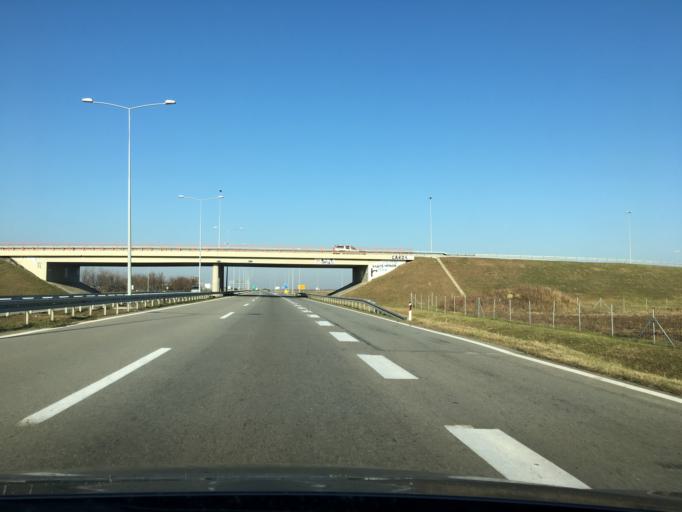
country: RS
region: Autonomna Pokrajina Vojvodina
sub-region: Juznobacki Okrug
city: Kovilj
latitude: 45.2422
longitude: 20.0355
